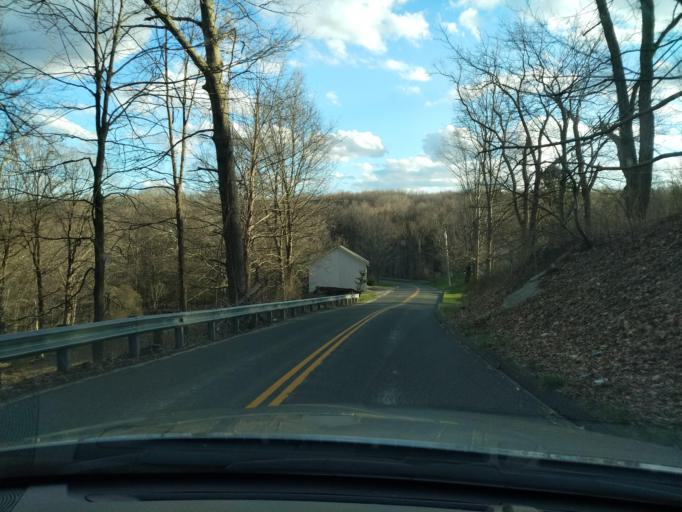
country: US
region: Connecticut
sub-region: Fairfield County
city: Newtown
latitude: 41.3791
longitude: -73.2833
